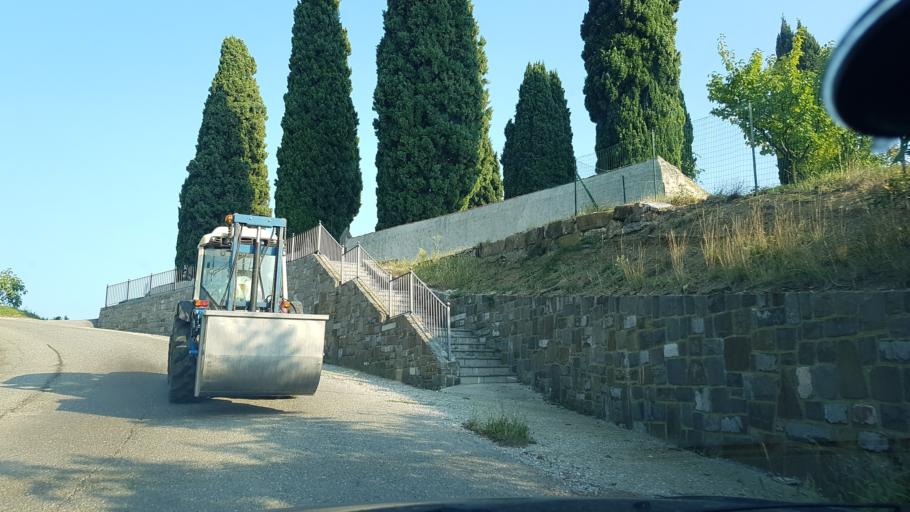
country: SI
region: Brda
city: Dobrovo
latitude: 45.9795
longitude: 13.5549
